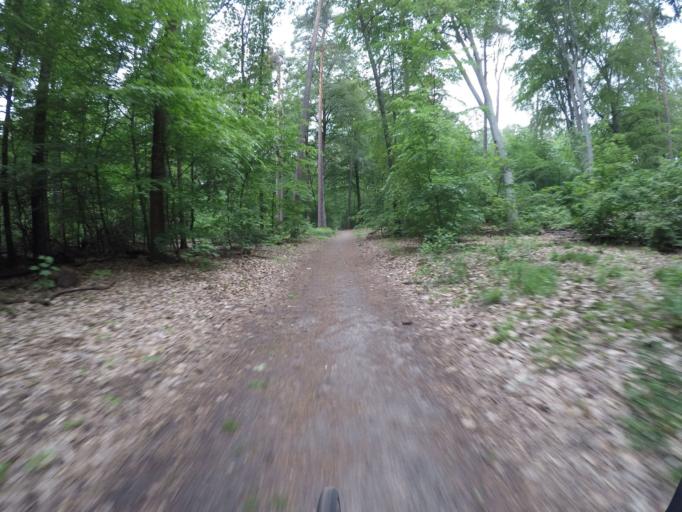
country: DE
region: Berlin
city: Frohnau
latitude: 52.6077
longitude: 13.2847
